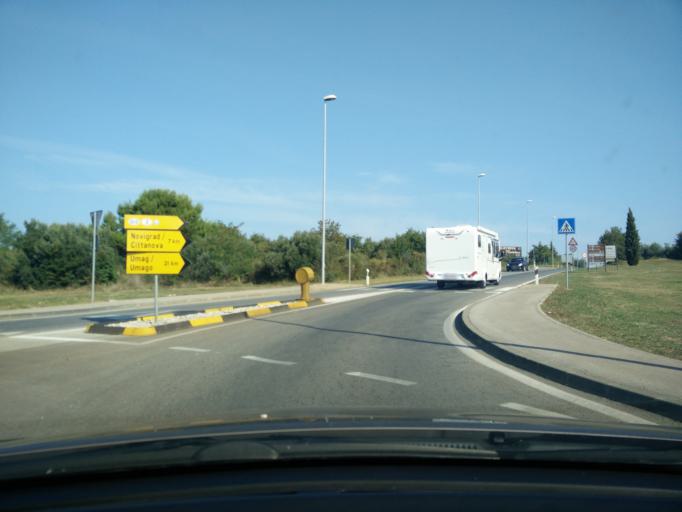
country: HR
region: Istarska
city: Novigrad
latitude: 45.2953
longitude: 13.6218
